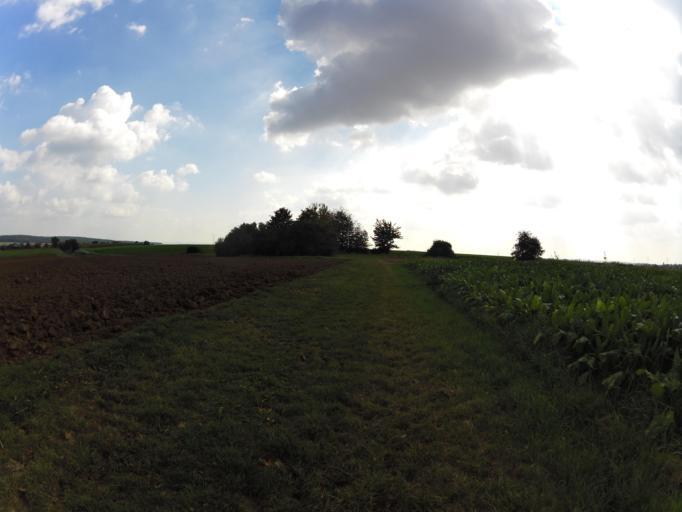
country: DE
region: Bavaria
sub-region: Regierungsbezirk Unterfranken
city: Prosselsheim
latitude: 49.8643
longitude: 10.1143
